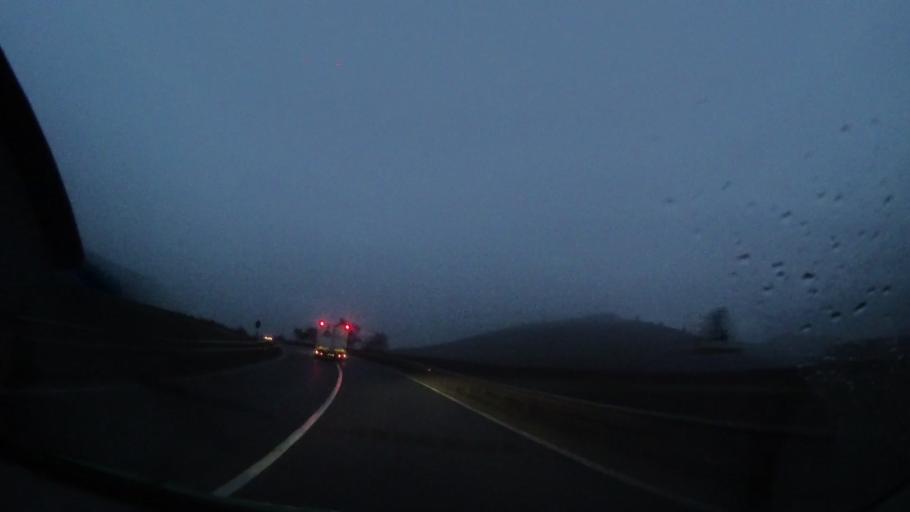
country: RO
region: Harghita
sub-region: Comuna Ditrau
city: Ditrau
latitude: 46.8372
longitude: 25.4891
